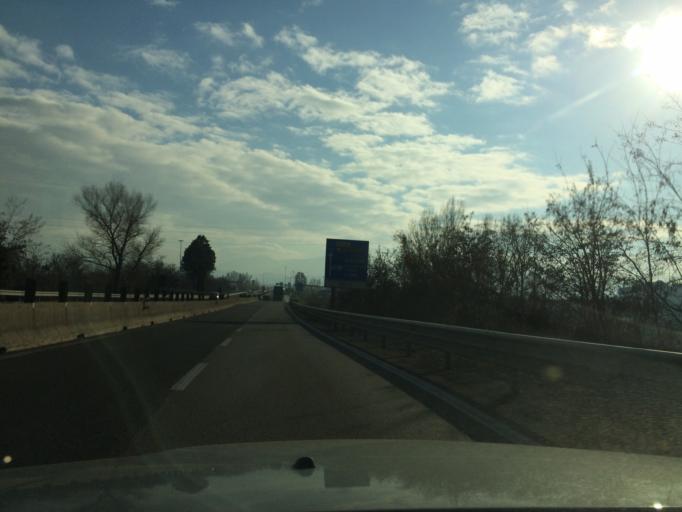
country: IT
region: Umbria
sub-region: Provincia di Terni
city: San Gemini
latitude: 42.5796
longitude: 12.5730
